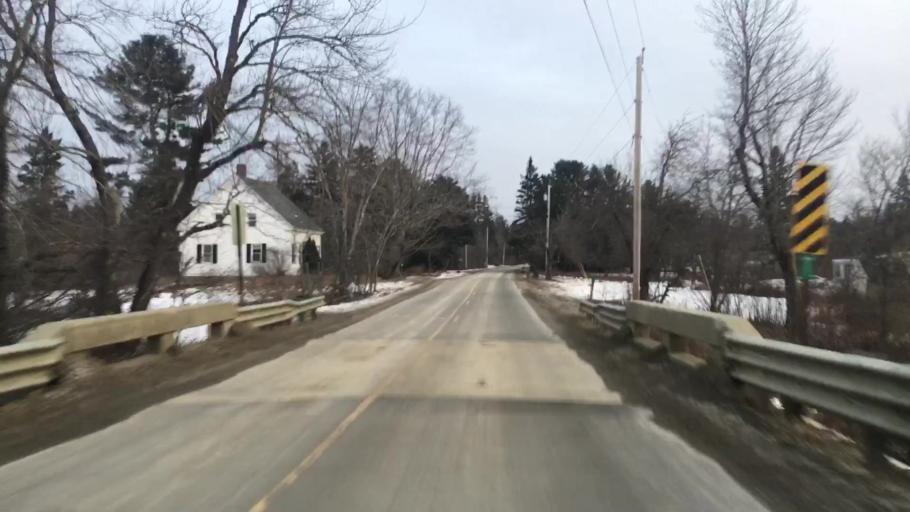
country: US
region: Maine
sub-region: Hancock County
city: Franklin
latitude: 44.6876
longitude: -68.3495
